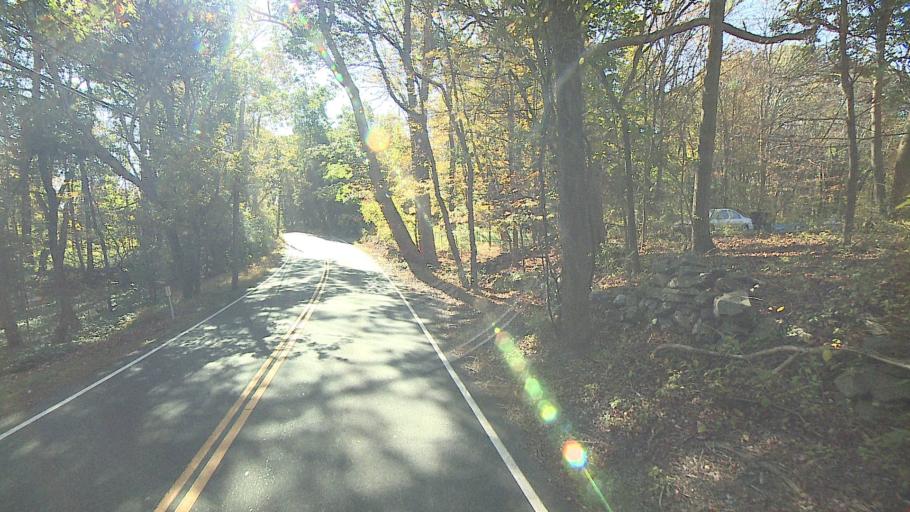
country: US
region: Connecticut
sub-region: Fairfield County
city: Trumbull
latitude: 41.2526
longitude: -73.3033
